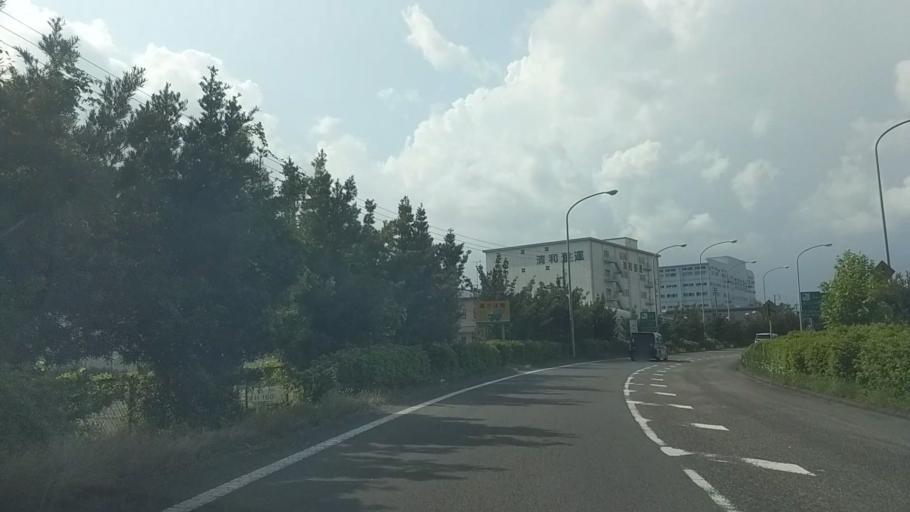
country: JP
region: Shizuoka
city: Hamakita
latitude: 34.7434
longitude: 137.7890
